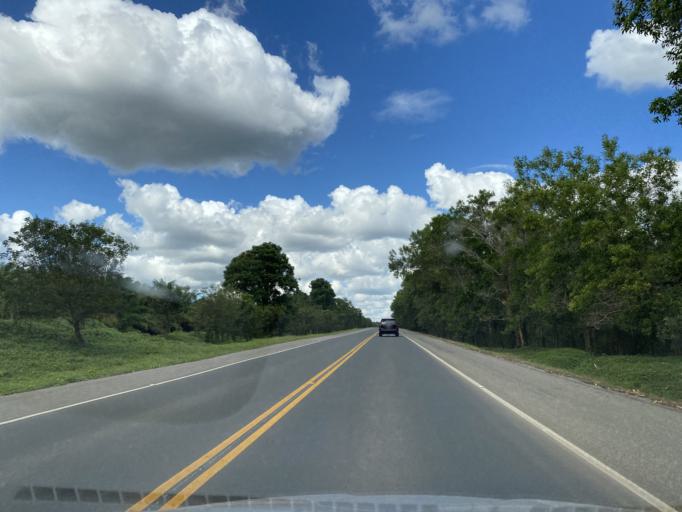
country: DO
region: Monte Plata
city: Monte Plata
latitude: 18.7039
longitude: -69.7541
